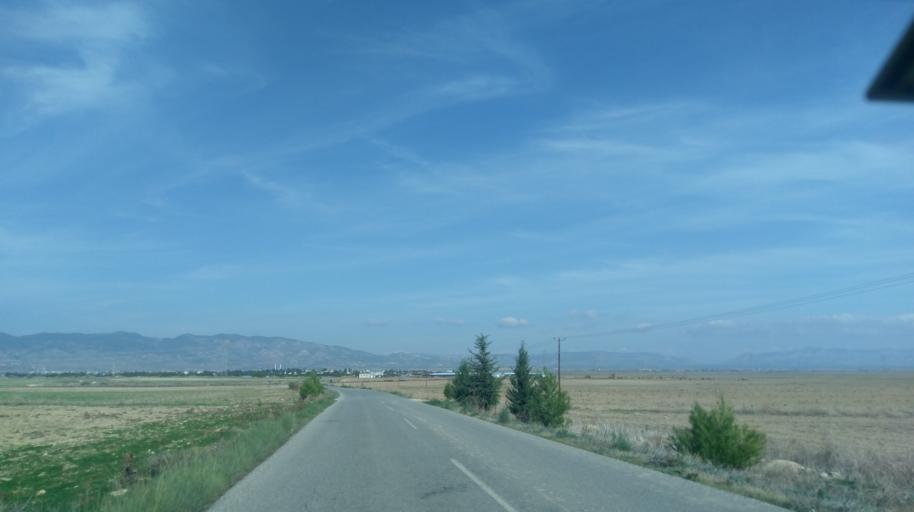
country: CY
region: Ammochostos
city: Lefkonoiko
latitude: 35.2006
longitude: 33.6193
